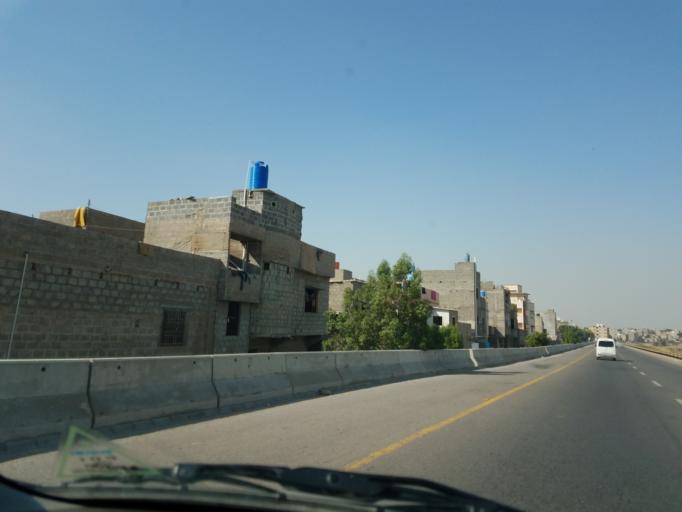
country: PK
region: Sindh
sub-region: Karachi District
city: Karachi
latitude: 24.9186
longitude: 67.0786
